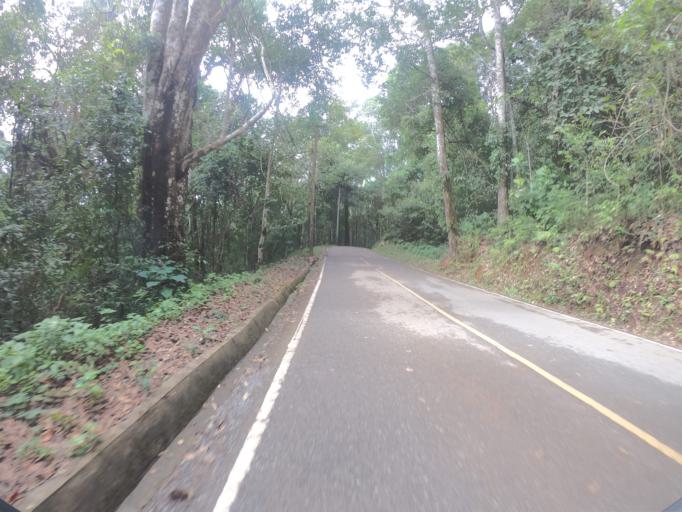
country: TH
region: Chiang Mai
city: Chiang Mai
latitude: 18.8102
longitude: 98.8904
